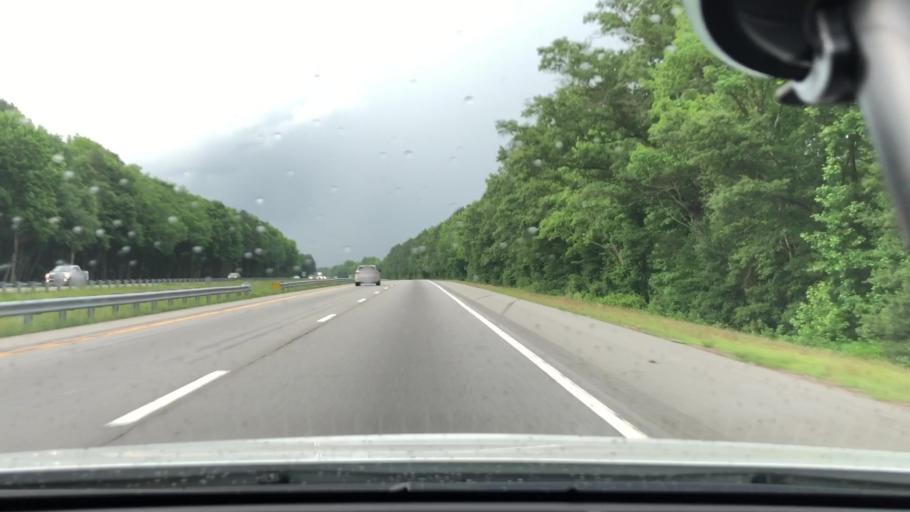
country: US
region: North Carolina
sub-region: Halifax County
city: Enfield
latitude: 36.2930
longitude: -77.7127
